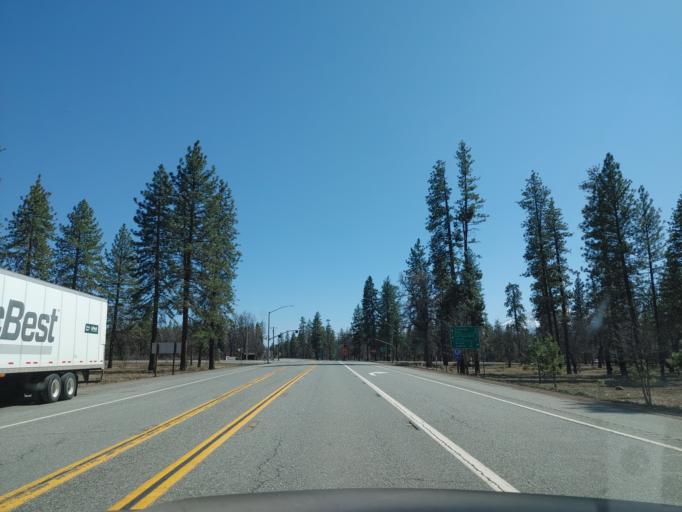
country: US
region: California
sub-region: Shasta County
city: Burney
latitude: 40.9395
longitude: -121.6072
